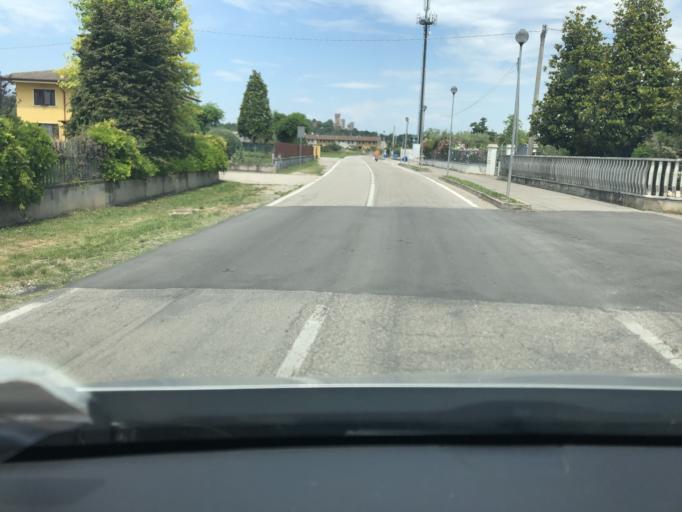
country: IT
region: Veneto
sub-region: Provincia di Verona
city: Valeggio sul Mincio
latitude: 45.3432
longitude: 10.7345
